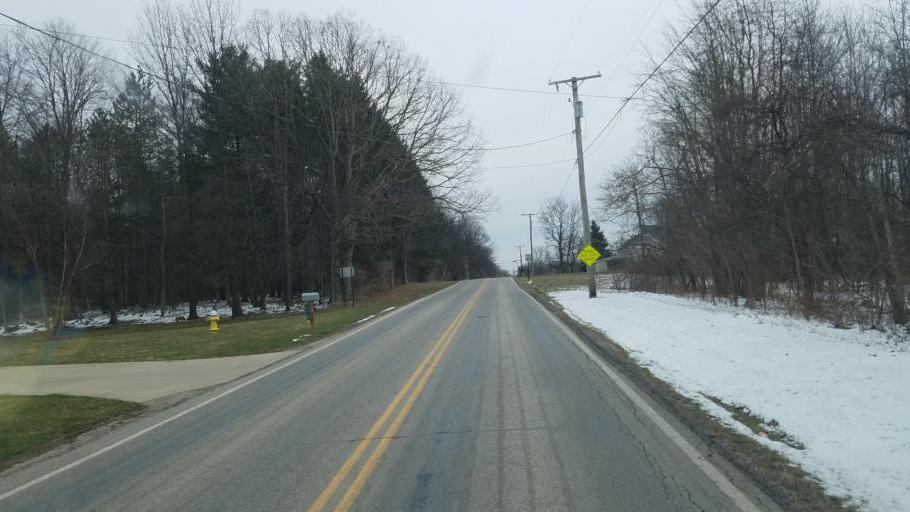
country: US
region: Ohio
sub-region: Richland County
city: Ontario
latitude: 40.7469
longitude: -82.5961
